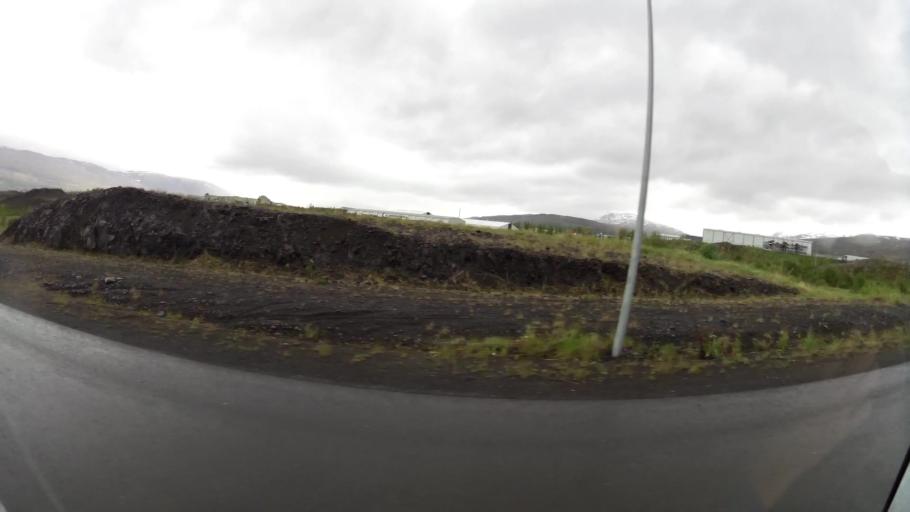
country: IS
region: Northeast
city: Akureyri
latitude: 65.7024
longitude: -18.1346
